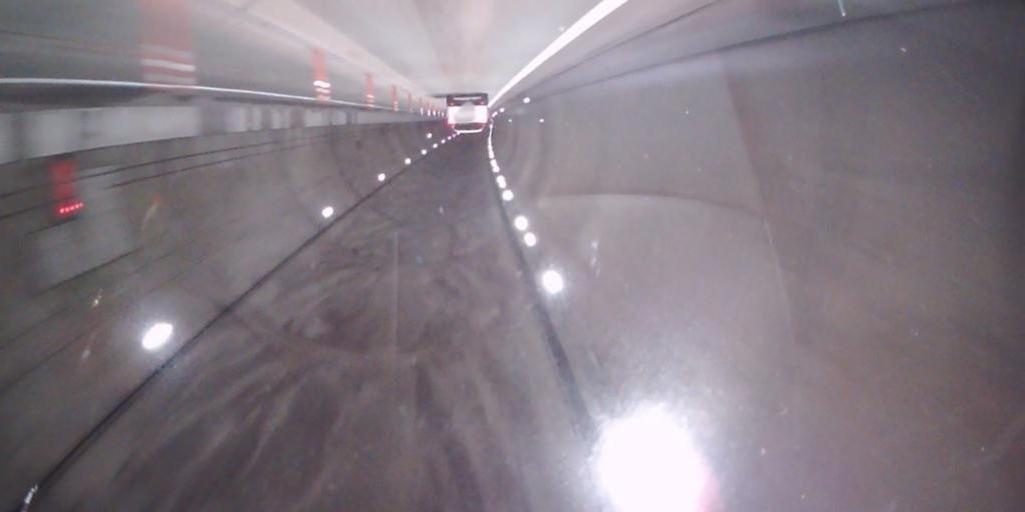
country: JP
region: Hokkaido
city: Date
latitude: 42.5735
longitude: 140.7444
